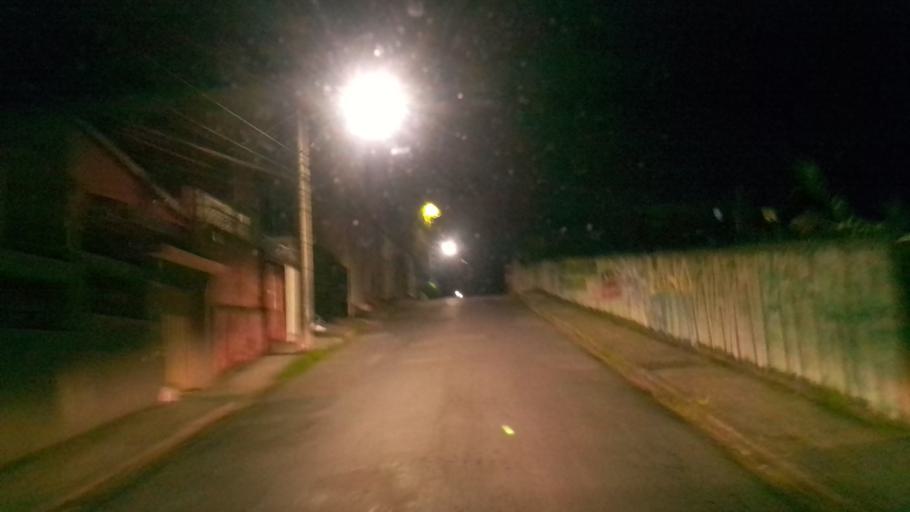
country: BR
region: Minas Gerais
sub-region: Belo Horizonte
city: Belo Horizonte
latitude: -19.9025
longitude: -43.9564
